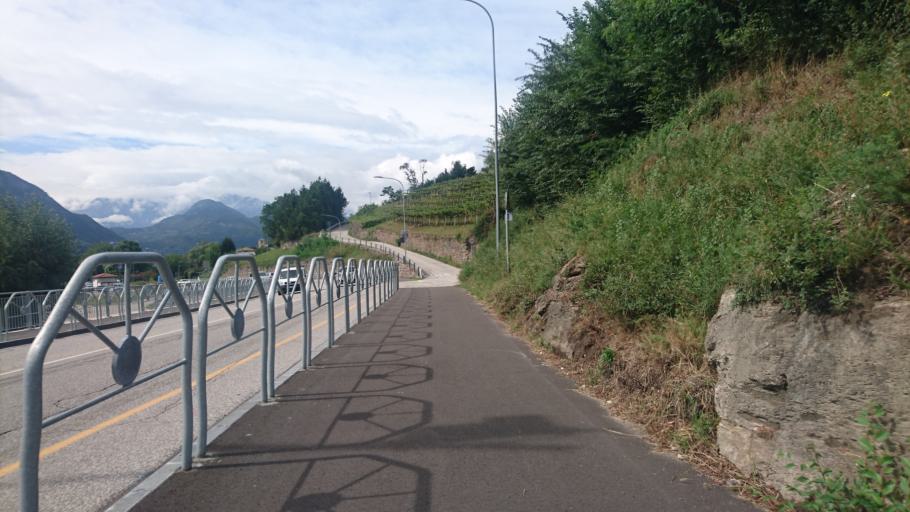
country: IT
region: Trentino-Alto Adige
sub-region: Provincia di Trento
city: Pergine Valsugana
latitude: 46.0696
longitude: 11.2239
